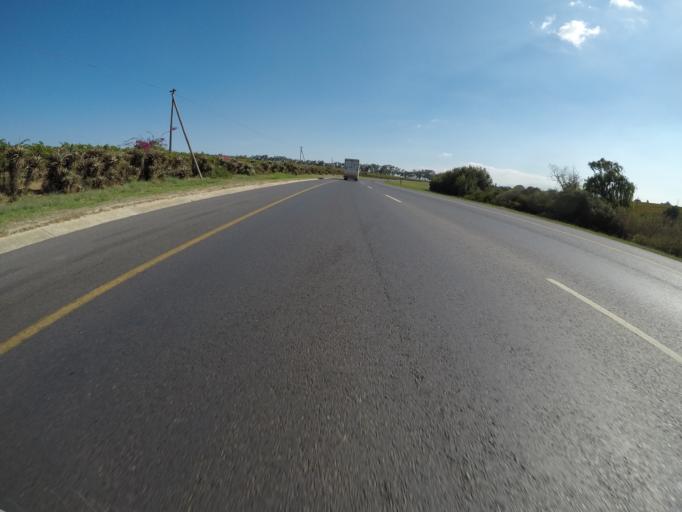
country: ZA
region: Western Cape
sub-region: City of Cape Town
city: Kraaifontein
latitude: -33.8975
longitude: 18.7329
